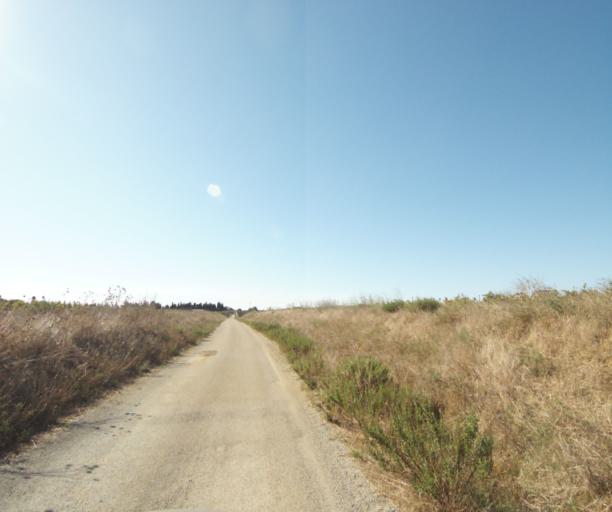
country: FR
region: Languedoc-Roussillon
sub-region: Departement du Gard
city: Bouillargues
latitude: 43.7869
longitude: 4.4105
